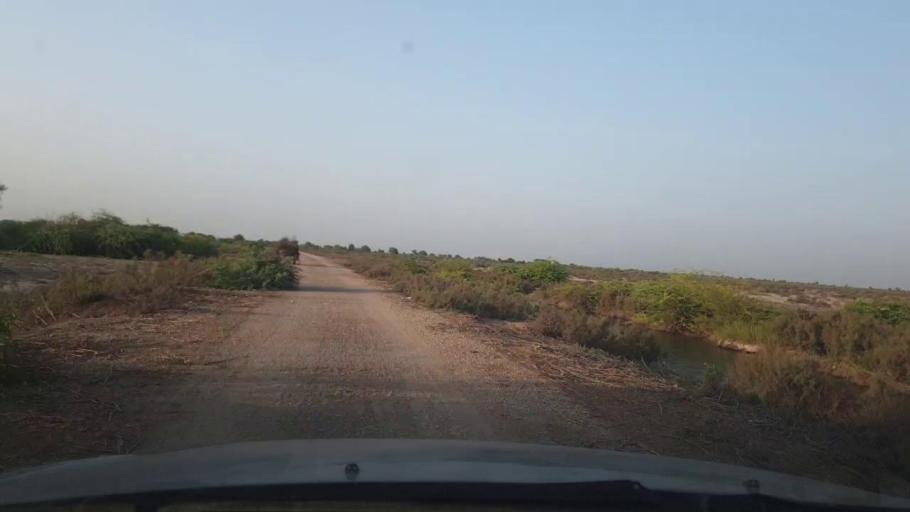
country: PK
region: Sindh
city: Tando Ghulam Ali
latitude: 25.1691
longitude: 68.9763
